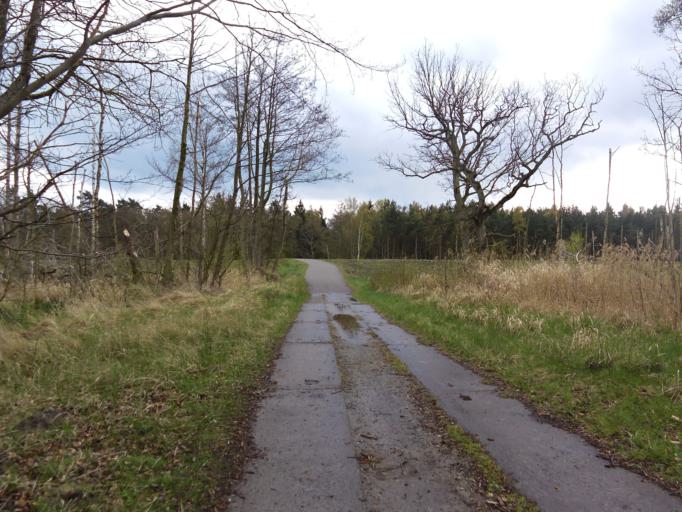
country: DE
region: Mecklenburg-Vorpommern
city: Zingst
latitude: 54.4374
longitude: 12.7798
